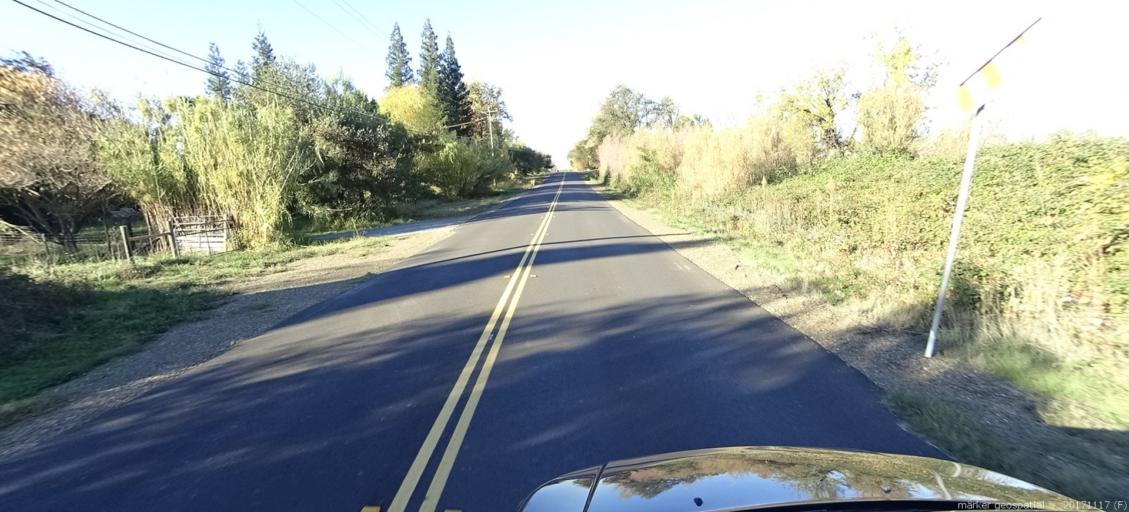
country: US
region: California
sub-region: Shasta County
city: Cottonwood
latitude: 40.3985
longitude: -122.2326
